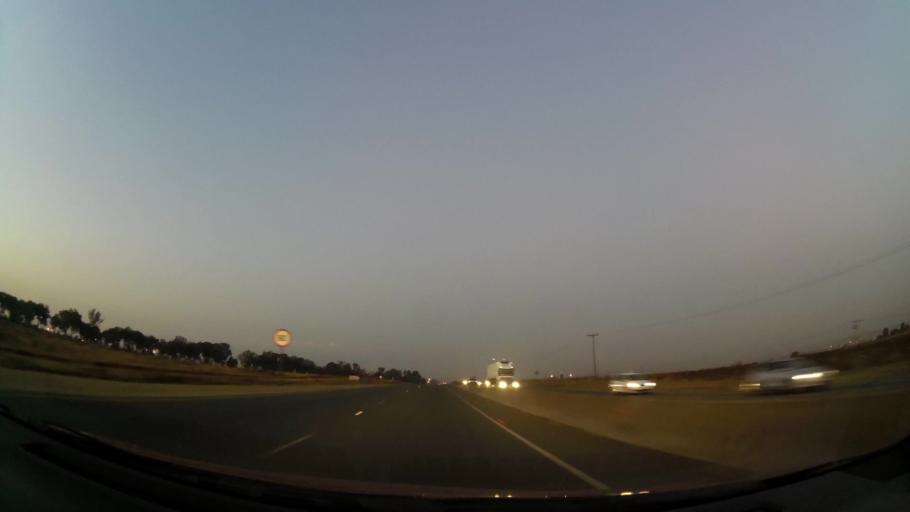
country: ZA
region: Gauteng
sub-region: City of Johannesburg Metropolitan Municipality
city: Soweto
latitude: -26.2957
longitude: 27.8293
